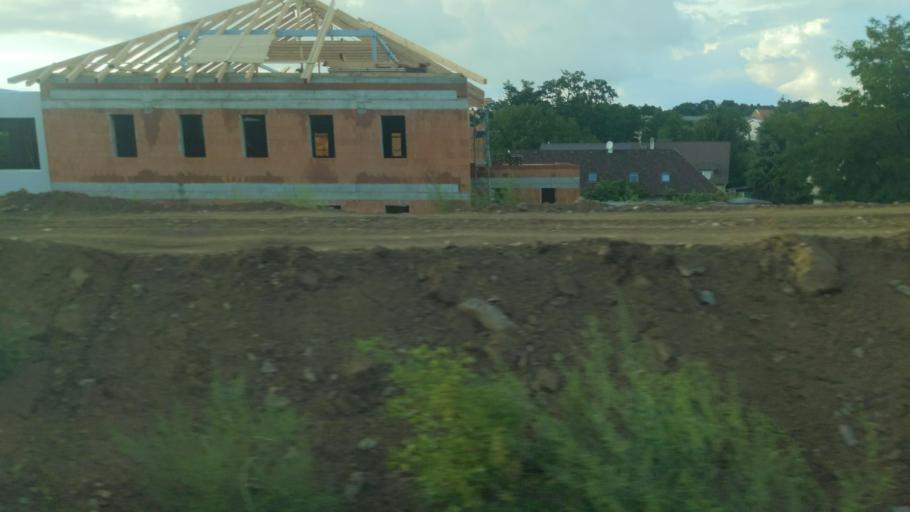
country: CZ
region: Central Bohemia
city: Uvaly
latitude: 50.0715
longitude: 14.7350
